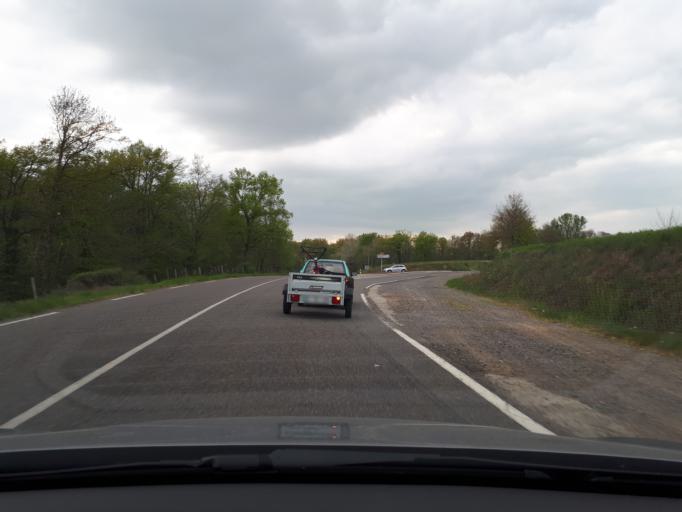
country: FR
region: Rhone-Alpes
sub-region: Departement de la Loire
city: Civens
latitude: 45.7424
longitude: 4.2782
